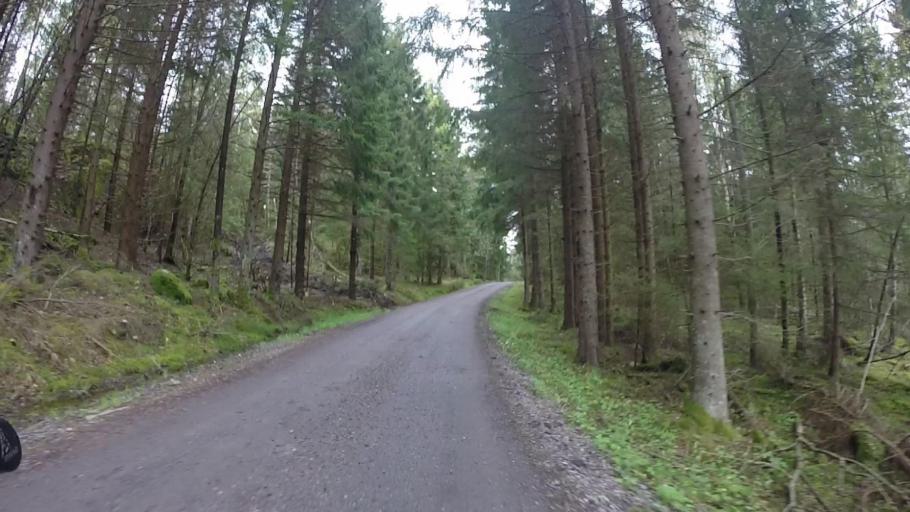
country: SE
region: Vaestra Goetaland
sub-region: Trollhattan
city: Sjuntorp
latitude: 58.2125
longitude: 12.2123
